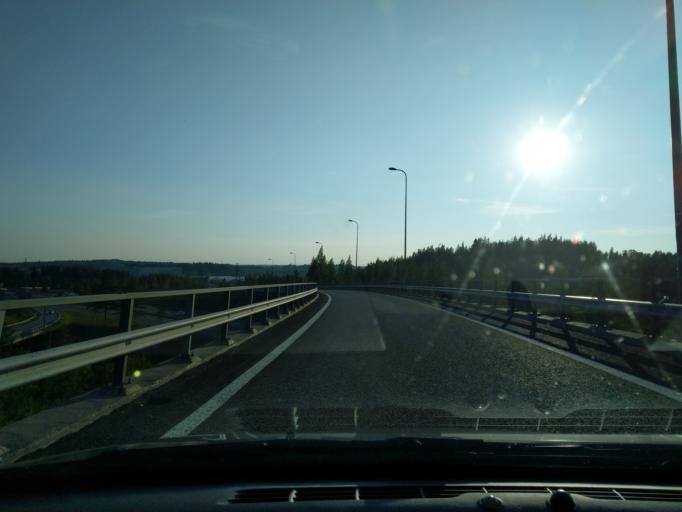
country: FI
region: Paijanne Tavastia
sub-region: Lahti
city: Lahti
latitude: 60.9705
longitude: 25.7219
